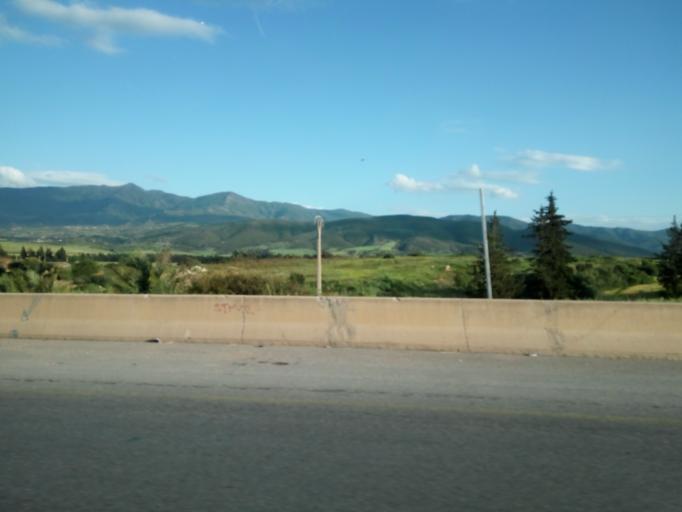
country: DZ
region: Tipaza
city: El Affroun
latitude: 36.4472
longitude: 2.6445
